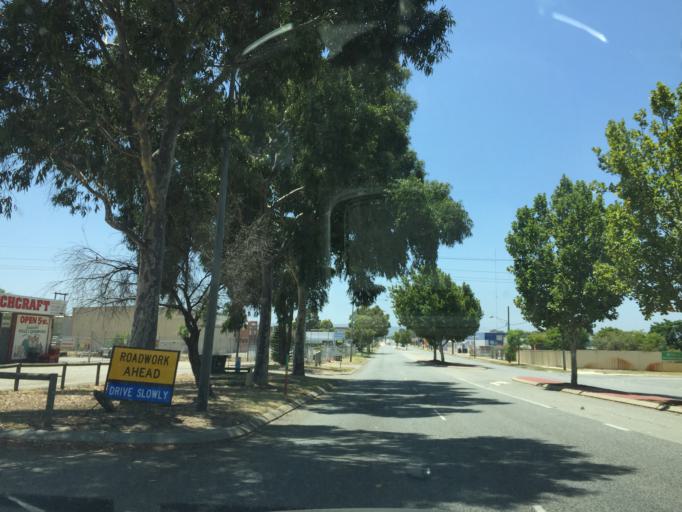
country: AU
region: Western Australia
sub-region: Canning
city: Queens Park
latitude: -31.9950
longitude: 115.9344
